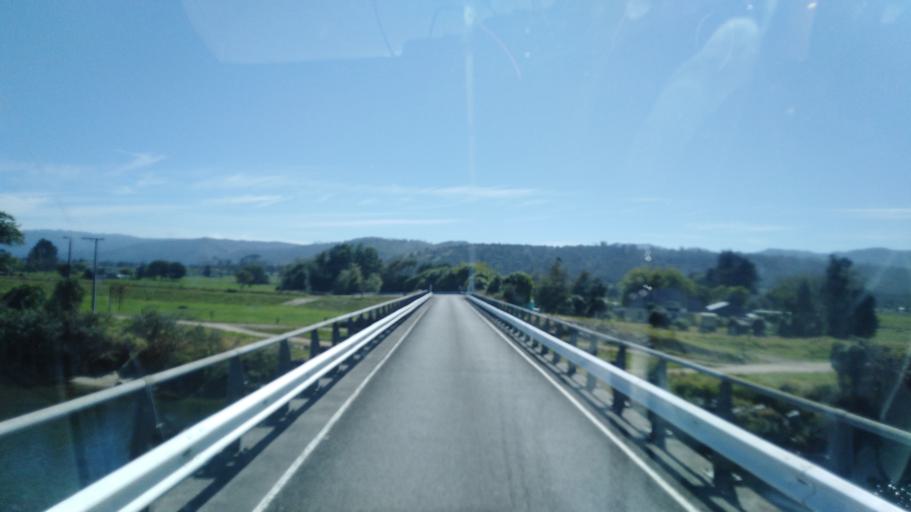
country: NZ
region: West Coast
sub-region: Buller District
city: Westport
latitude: -41.2610
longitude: 172.1312
